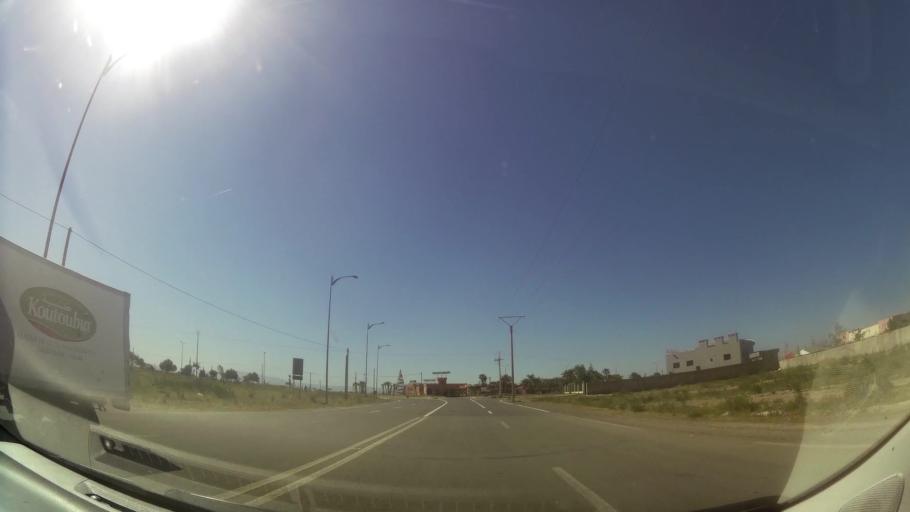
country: MA
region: Oriental
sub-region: Oujda-Angad
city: Oujda
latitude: 34.7312
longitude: -1.8723
